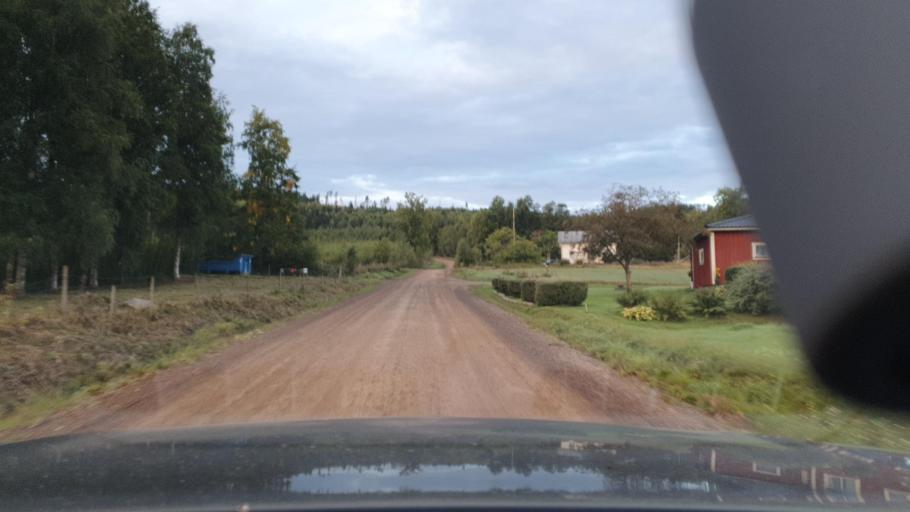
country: SE
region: Vaermland
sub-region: Sunne Kommun
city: Sunne
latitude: 59.8470
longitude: 12.9426
